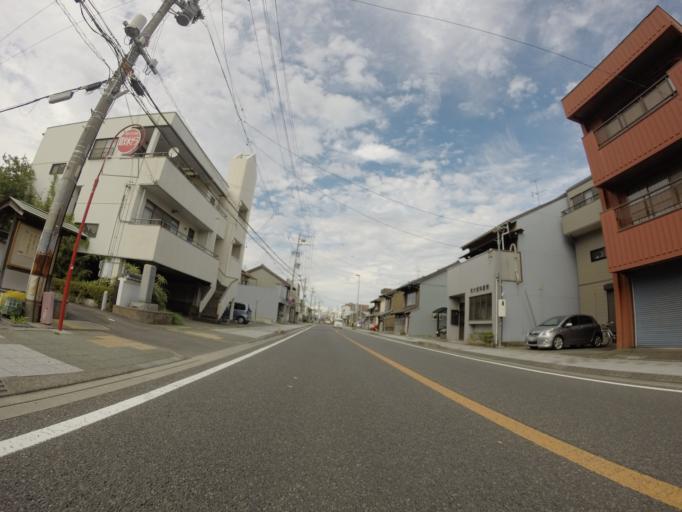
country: JP
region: Shizuoka
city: Shizuoka-shi
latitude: 35.0505
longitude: 138.5208
